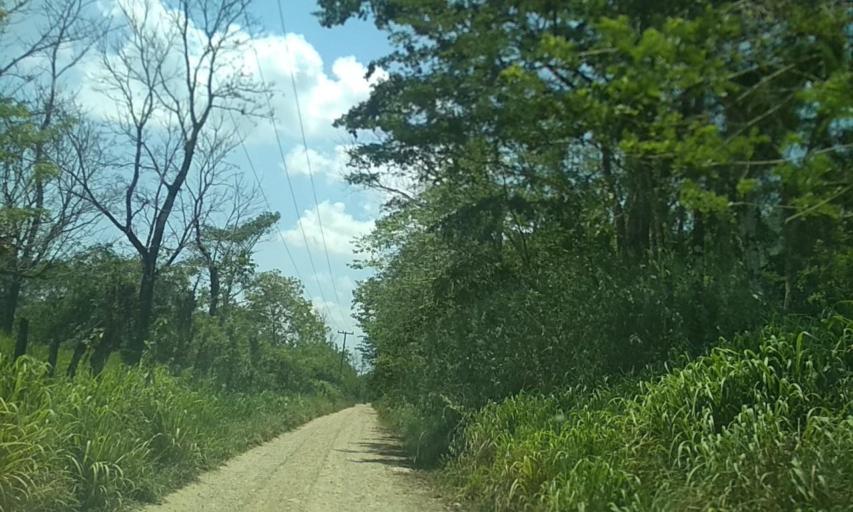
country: MX
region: Chiapas
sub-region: Tecpatan
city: Raudales Malpaso
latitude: 17.2850
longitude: -93.8371
